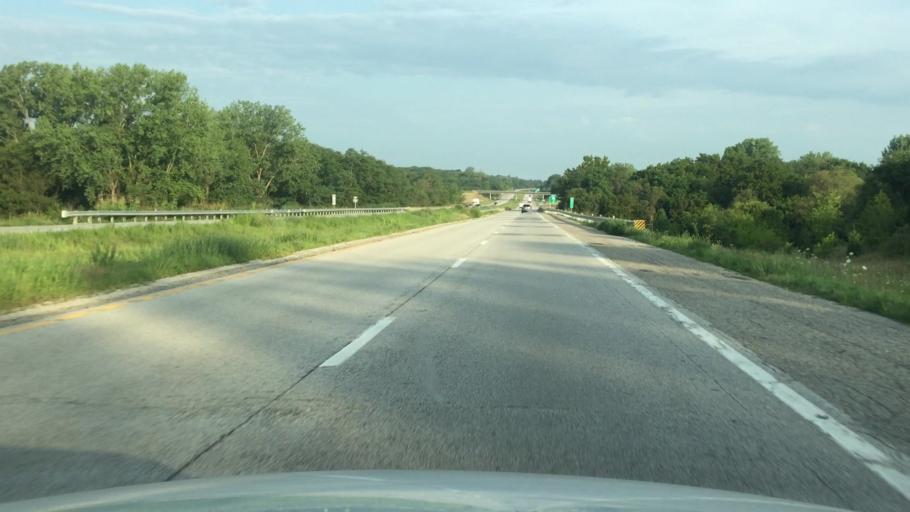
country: US
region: Missouri
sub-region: Buchanan County
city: Saint Joseph
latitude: 39.7144
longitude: -94.8116
